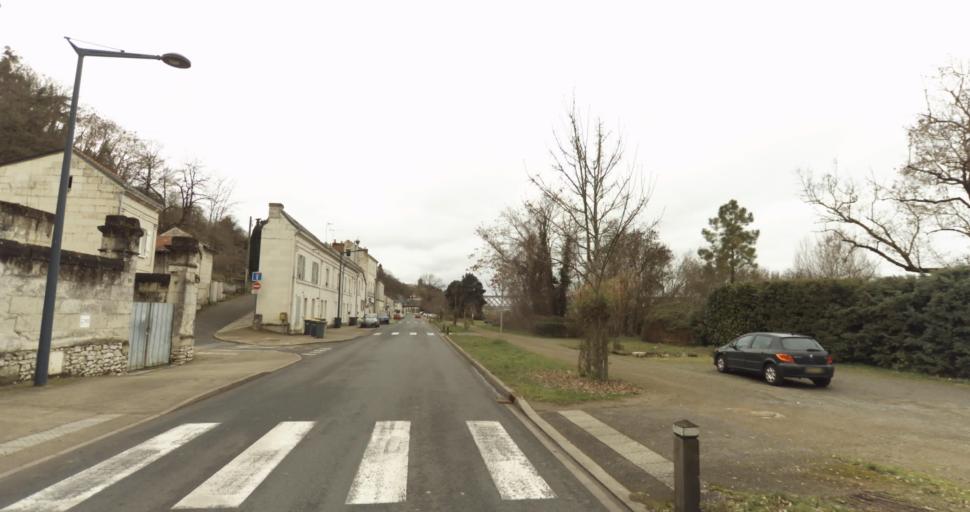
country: FR
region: Pays de la Loire
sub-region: Departement de Maine-et-Loire
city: Villebernier
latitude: 47.2508
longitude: -0.0558
